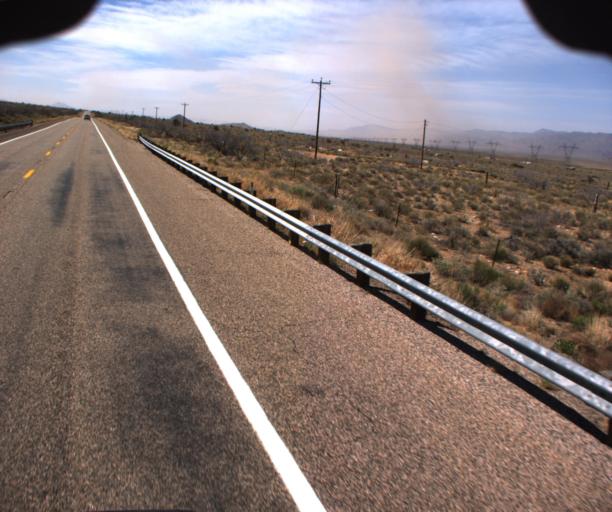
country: US
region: Arizona
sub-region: Mohave County
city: New Kingman-Butler
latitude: 35.4010
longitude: -113.7604
